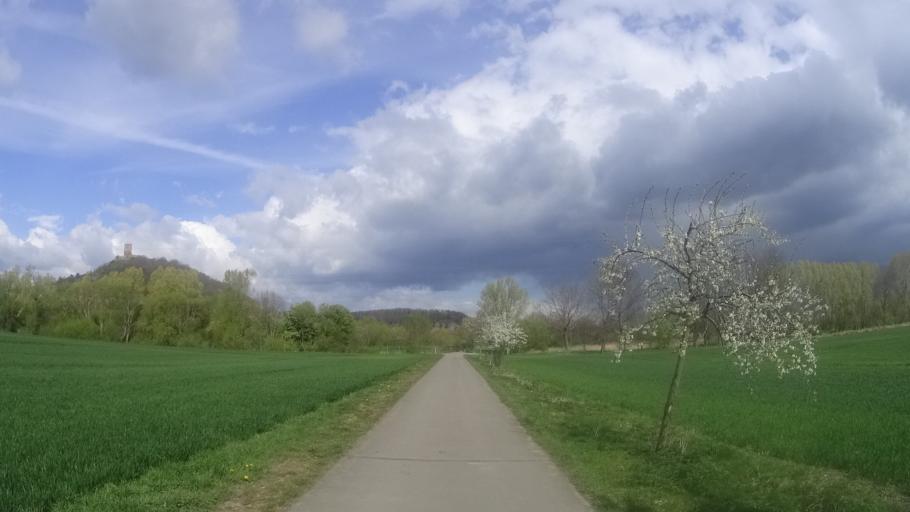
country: DE
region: Thuringia
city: Wandersleben
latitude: 50.8762
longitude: 10.8479
